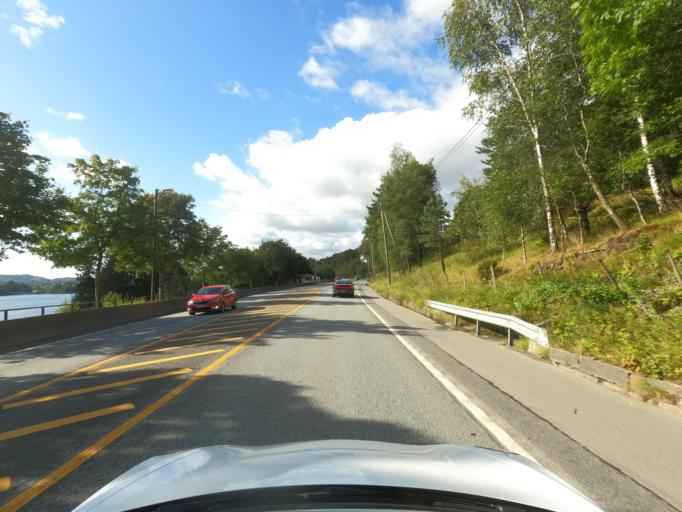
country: NO
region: Hordaland
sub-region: Bergen
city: Bergen
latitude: 60.3431
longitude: 5.3312
